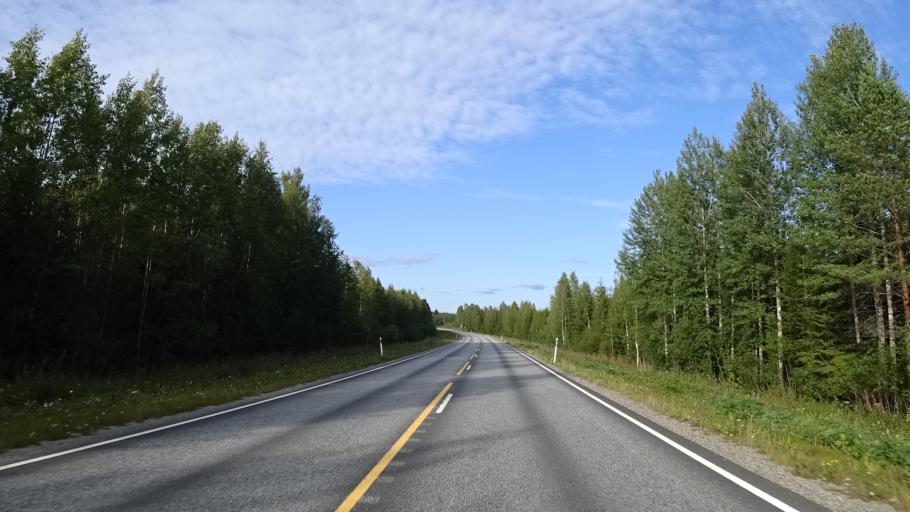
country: FI
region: North Karelia
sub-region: Joensuu
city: Eno
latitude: 62.8153
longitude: 30.1809
